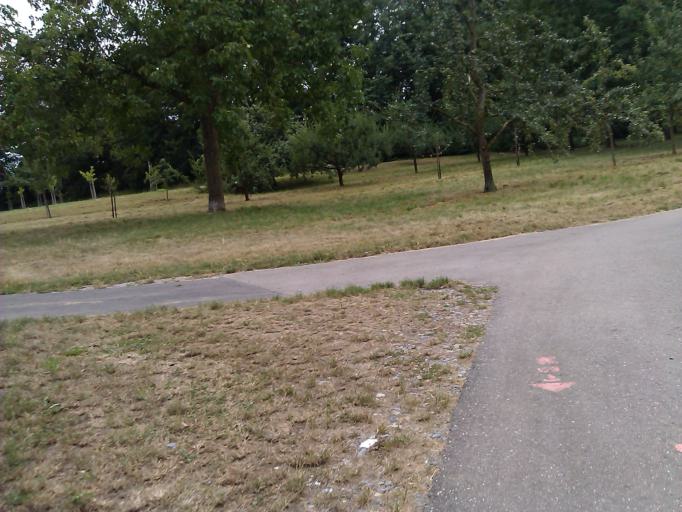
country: DE
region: Baden-Wuerttemberg
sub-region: Regierungsbezirk Stuttgart
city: Talheim
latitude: 49.1115
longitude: 9.1808
